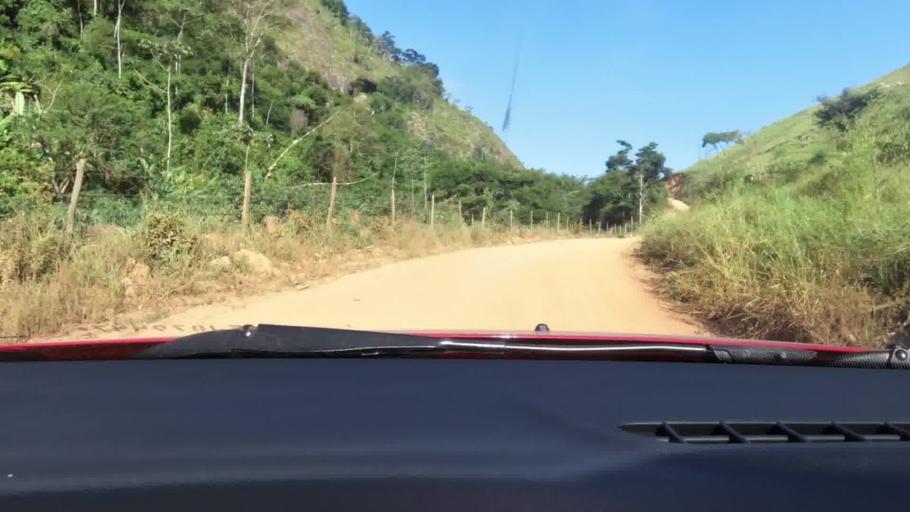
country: BR
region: Espirito Santo
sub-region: Guarapari
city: Guarapari
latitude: -20.5257
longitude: -40.5654
